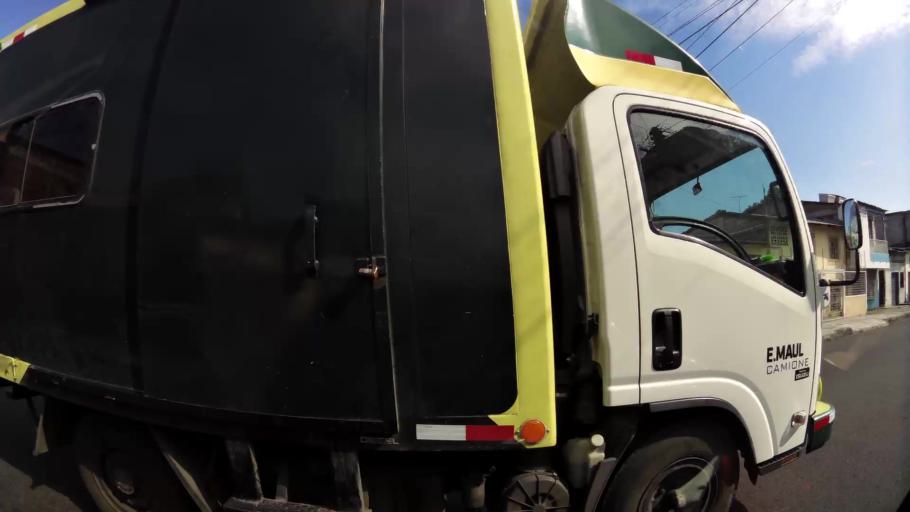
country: EC
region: Guayas
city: Guayaquil
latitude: -2.2140
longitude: -79.9107
